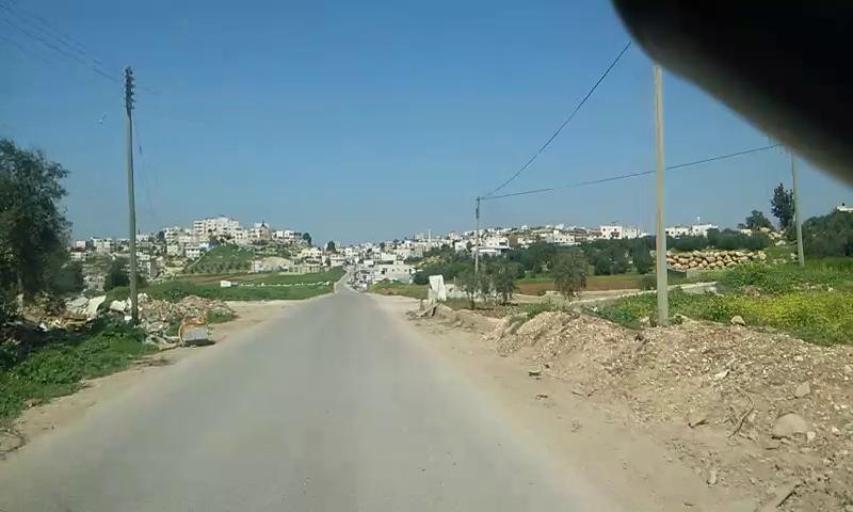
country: PS
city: Dayr Samit
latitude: 31.5131
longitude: 34.9705
